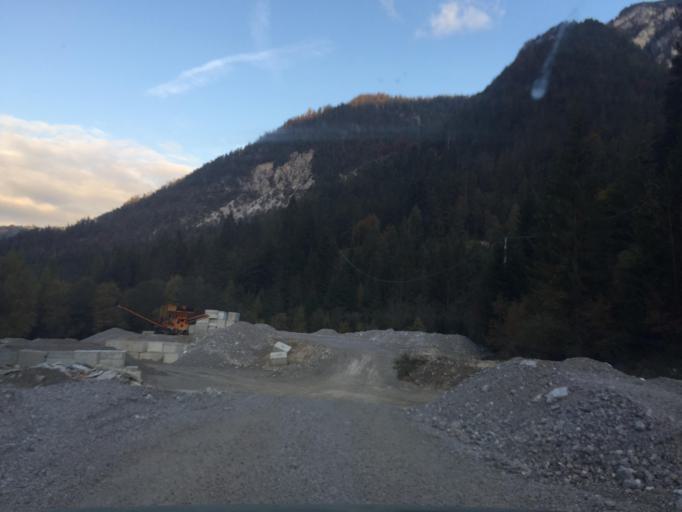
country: IT
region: Veneto
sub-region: Provincia di Belluno
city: San Pietro di Cadore
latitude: 46.5817
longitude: 12.6280
